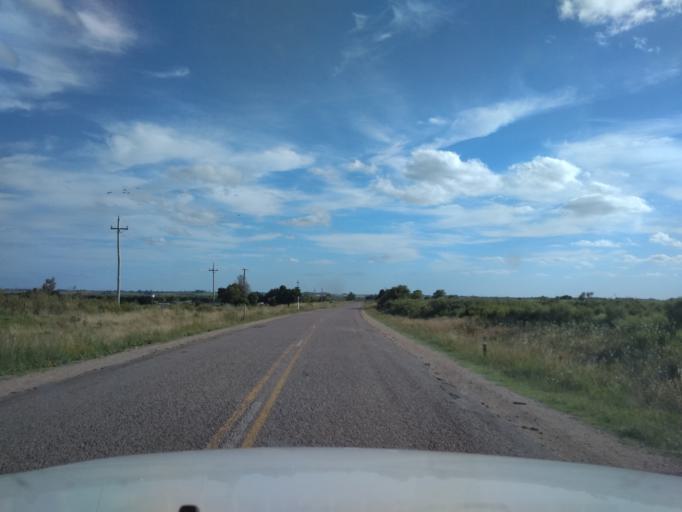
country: UY
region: Canelones
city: San Ramon
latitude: -34.2598
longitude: -55.9271
